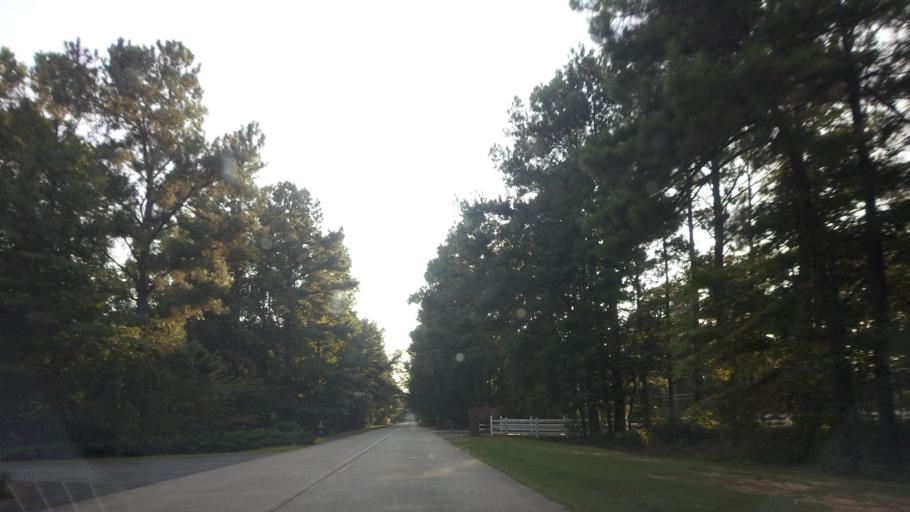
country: US
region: Georgia
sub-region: Bibb County
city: Macon
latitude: 32.9425
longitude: -83.7505
